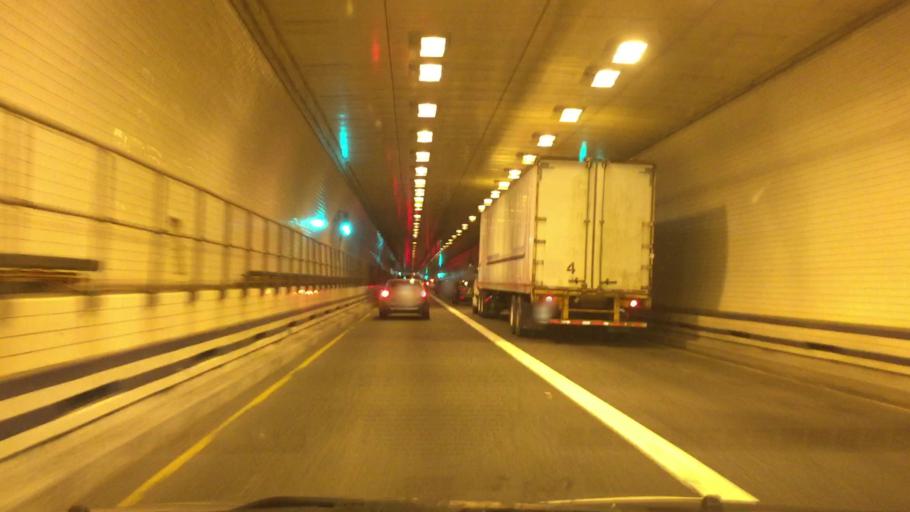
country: US
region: Virginia
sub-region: City of Newport News
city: Newport News
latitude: 36.9570
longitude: -76.4096
